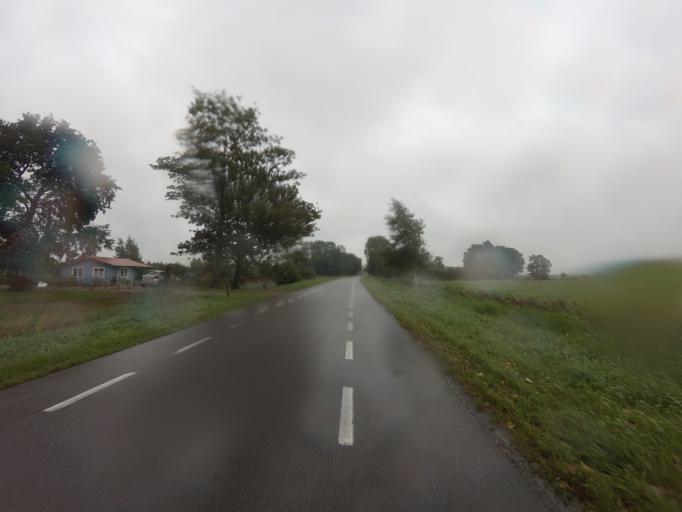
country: NL
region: Friesland
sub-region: Gemeente Smallingerland
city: Oudega
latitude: 53.0965
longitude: 5.9666
